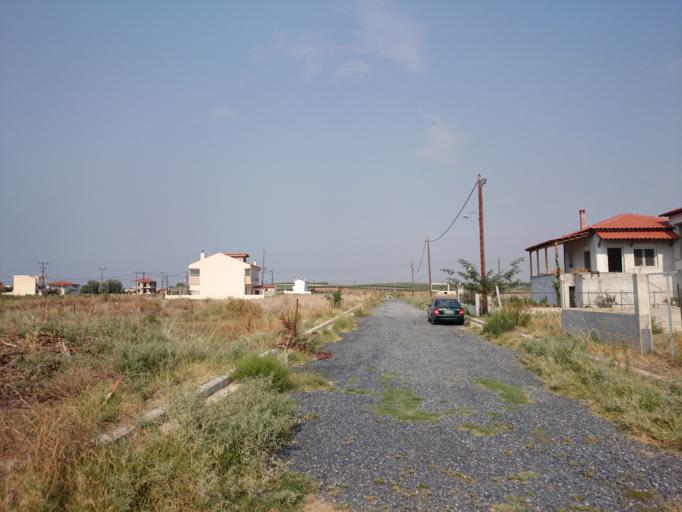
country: GR
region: Central Macedonia
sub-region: Nomos Chalkidikis
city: Nea Moudhania
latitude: 40.2525
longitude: 23.2560
